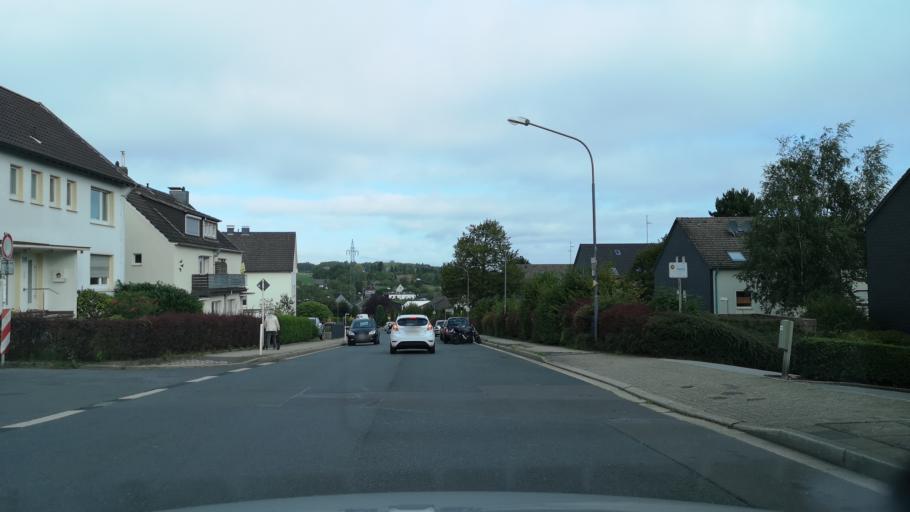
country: DE
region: North Rhine-Westphalia
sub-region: Regierungsbezirk Dusseldorf
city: Wuppertal
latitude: 51.3007
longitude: 7.1612
